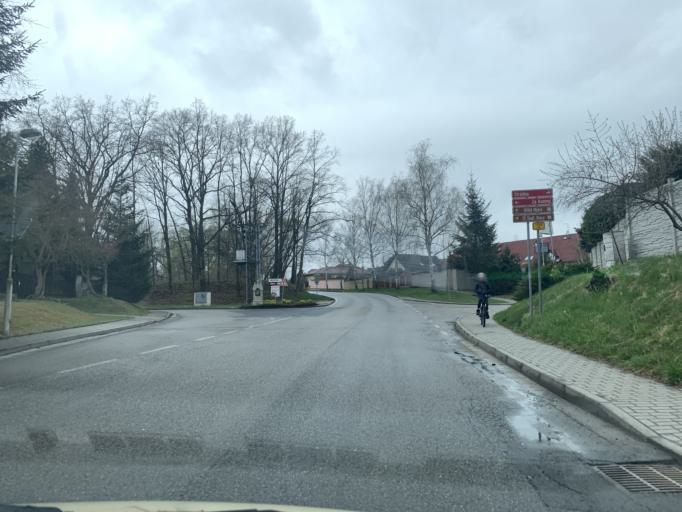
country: CZ
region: Jihocesky
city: Litvinovice
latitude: 48.9621
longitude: 14.4479
